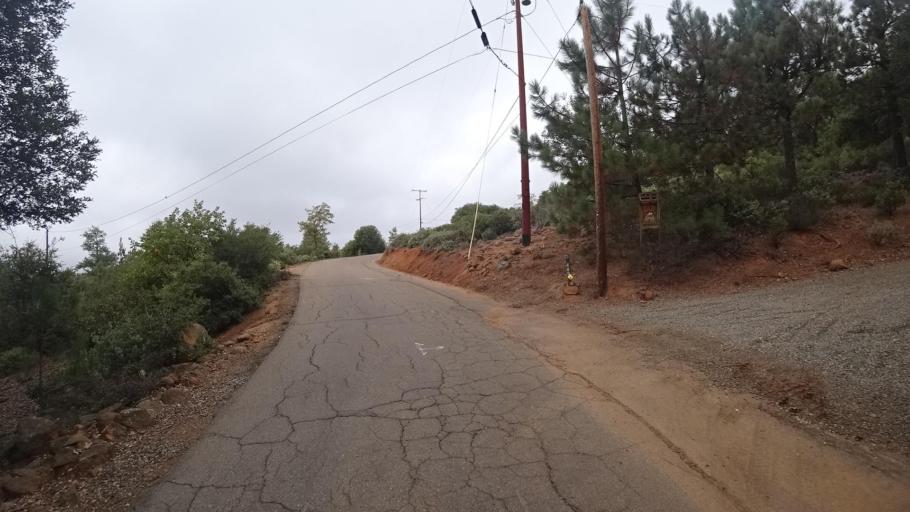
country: US
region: California
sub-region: San Diego County
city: Julian
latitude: 33.0444
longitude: -116.6306
